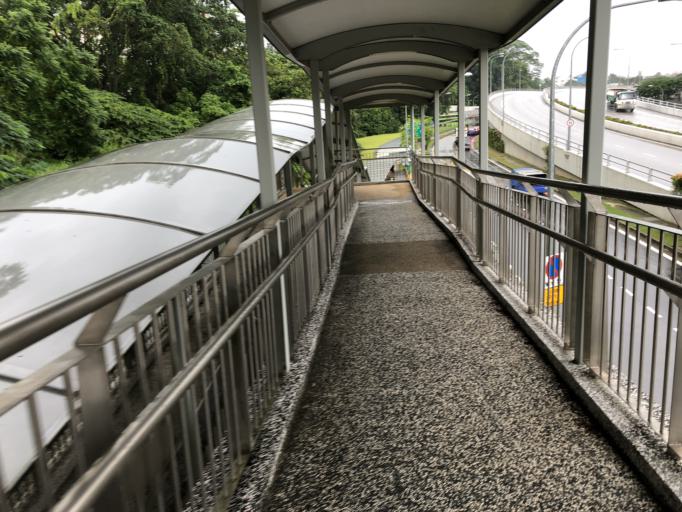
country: MY
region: Johor
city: Johor Bahru
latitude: 1.3599
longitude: 103.7669
